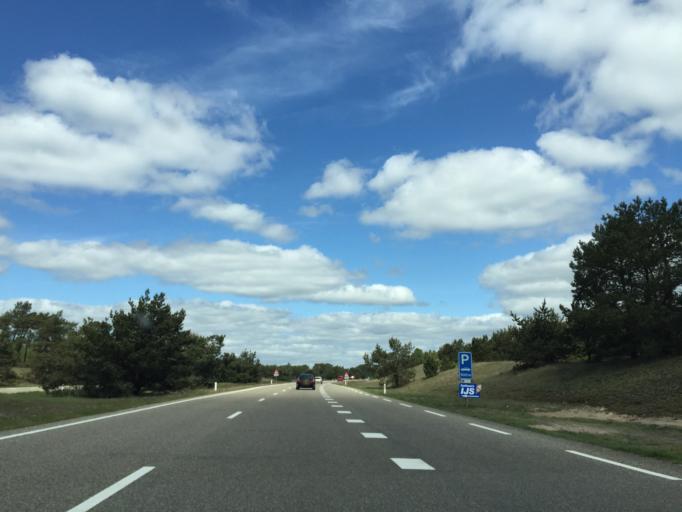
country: NL
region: Gelderland
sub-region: Gemeente Apeldoorn
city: Uddel
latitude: 52.2009
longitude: 5.7782
